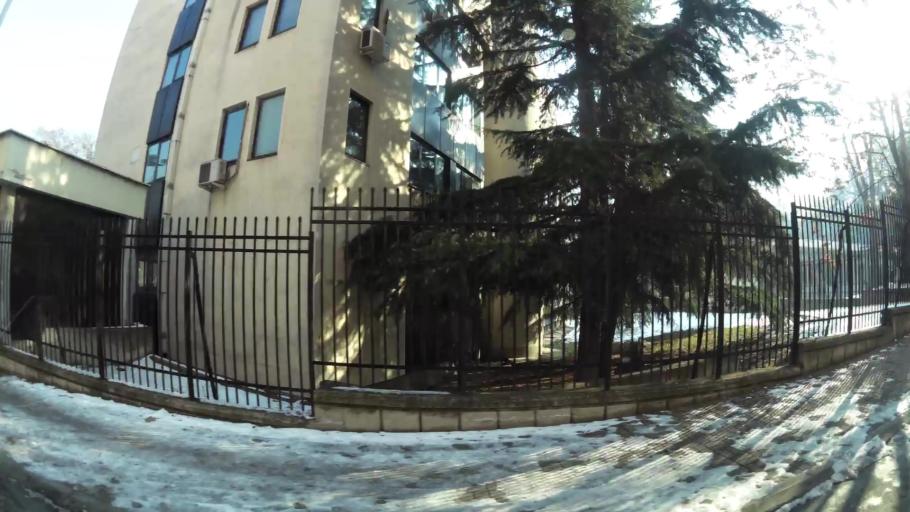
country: MK
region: Karpos
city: Skopje
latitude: 41.9868
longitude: 21.4274
